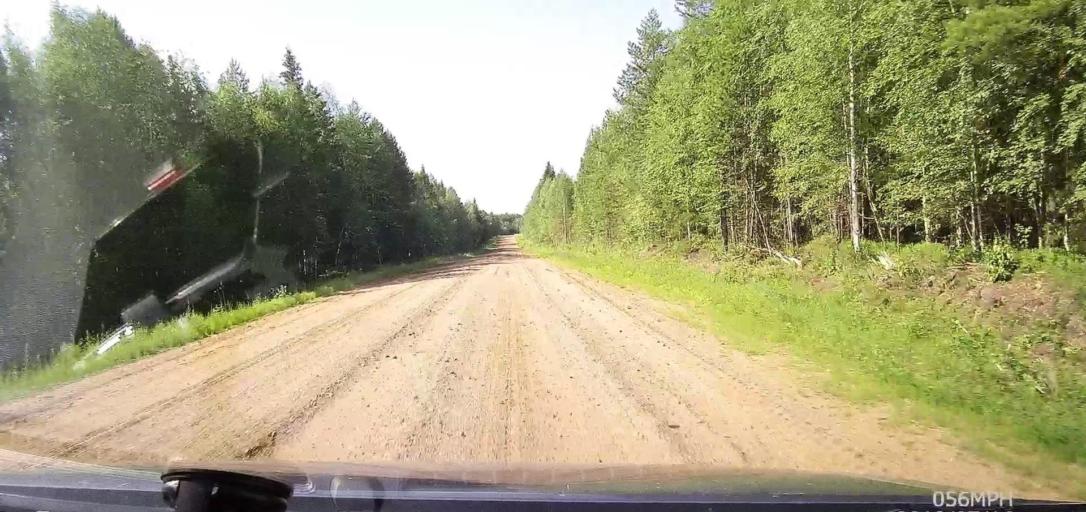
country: RU
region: Arkhangelskaya
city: Leshukonskoye
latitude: 65.4296
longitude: 45.0661
